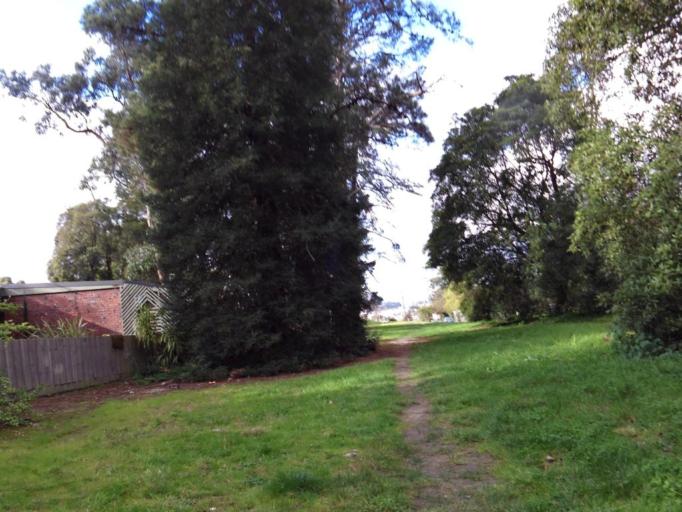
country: AU
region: Victoria
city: Mitcham
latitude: -37.8182
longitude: 145.2115
